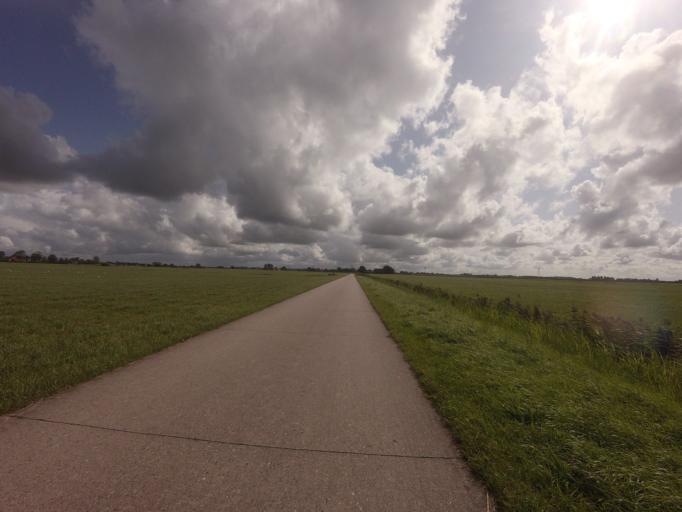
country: NL
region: Friesland
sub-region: Sudwest Fryslan
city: Scharnegoutum
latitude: 53.0697
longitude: 5.6380
